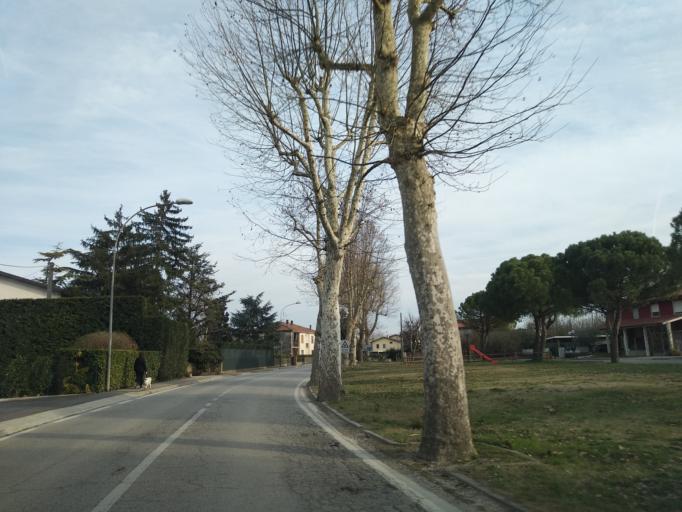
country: IT
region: Veneto
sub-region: Provincia di Vicenza
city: Ponte di Barbarano
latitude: 45.3951
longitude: 11.5691
